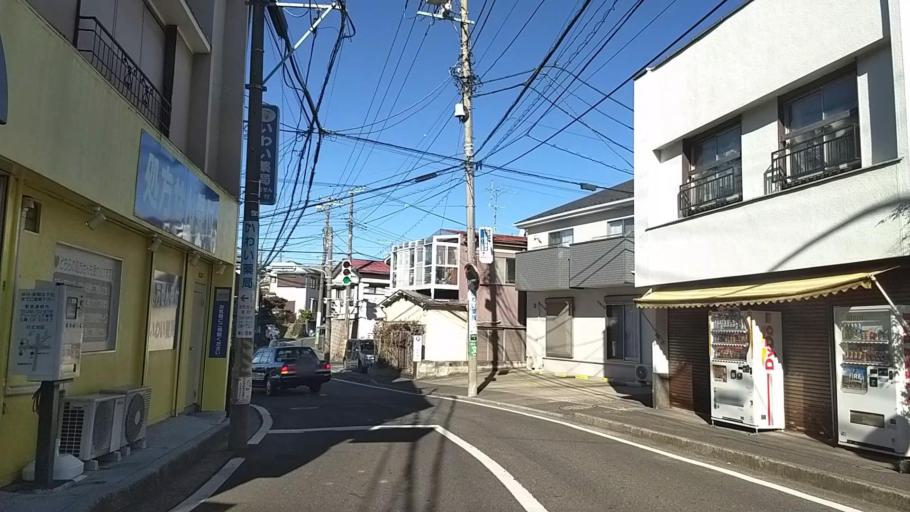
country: JP
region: Kanagawa
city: Yokohama
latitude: 35.4438
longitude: 139.6039
